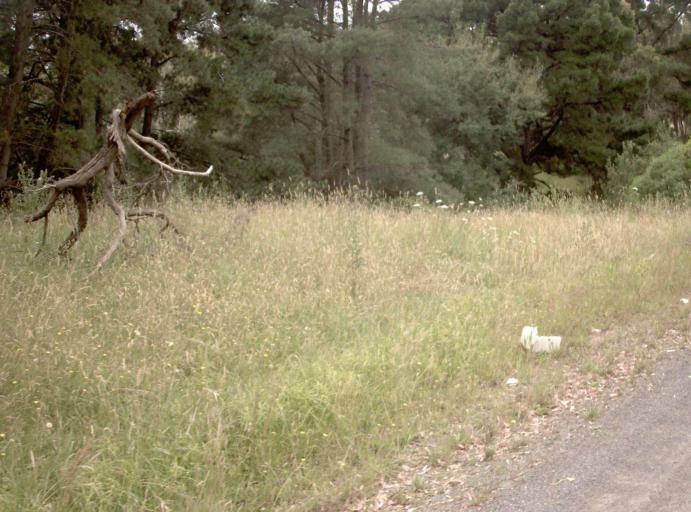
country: AU
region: Victoria
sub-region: Yarra Ranges
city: Mount Evelyn
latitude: -37.7602
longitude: 145.3941
